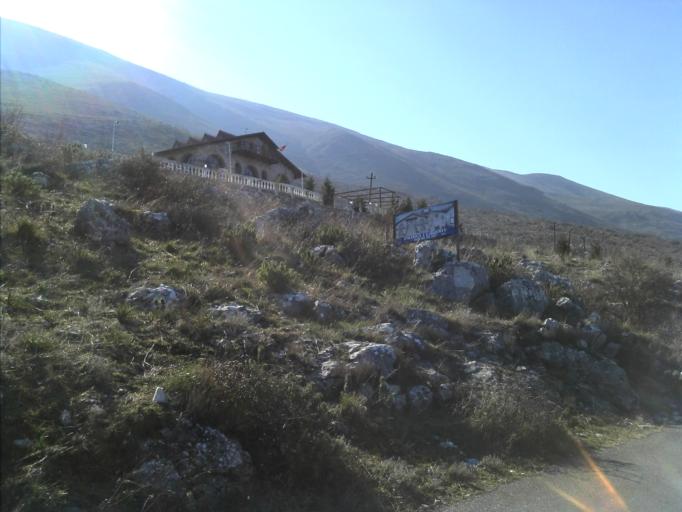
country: AL
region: Shkoder
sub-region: Rrethi i Shkodres
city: Dajc
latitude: 42.0679
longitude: 19.4246
